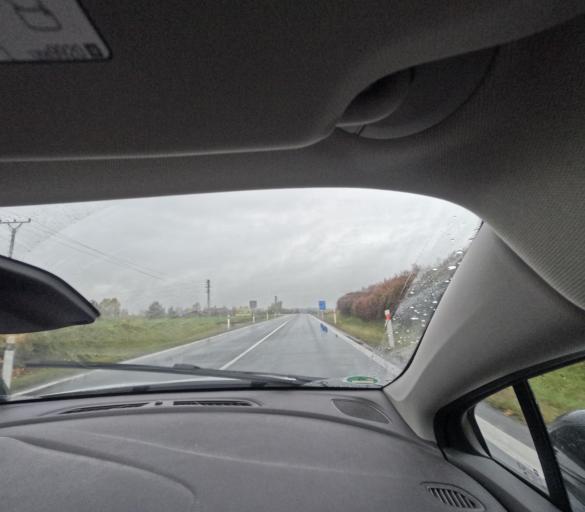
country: CZ
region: Central Bohemia
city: Velka Dobra
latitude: 50.1062
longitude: 14.0791
